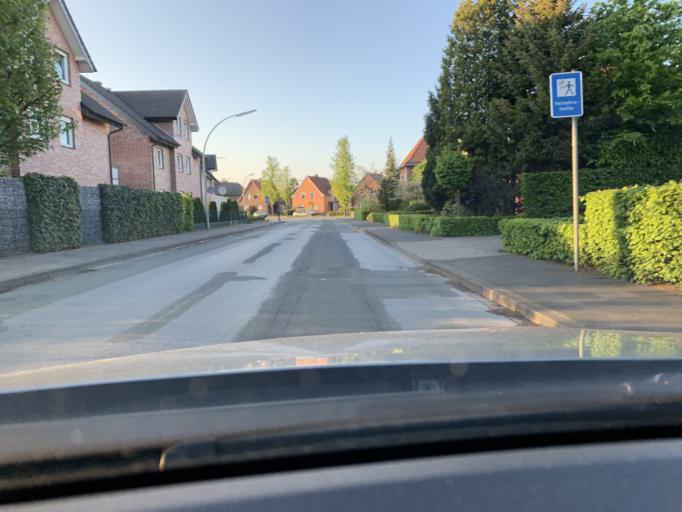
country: DE
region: North Rhine-Westphalia
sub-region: Regierungsbezirk Detmold
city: Rheda-Wiedenbruck
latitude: 51.8393
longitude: 8.3221
